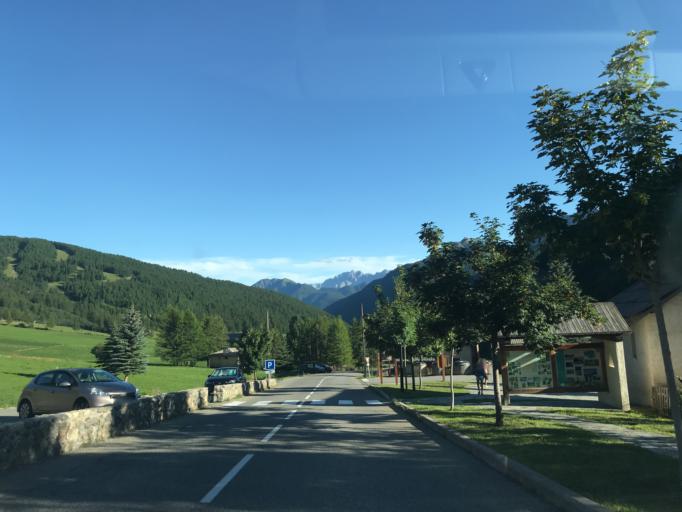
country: FR
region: Provence-Alpes-Cote d'Azur
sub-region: Departement des Hautes-Alpes
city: Villar-Saint-Pancrace
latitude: 44.7925
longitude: 6.7317
